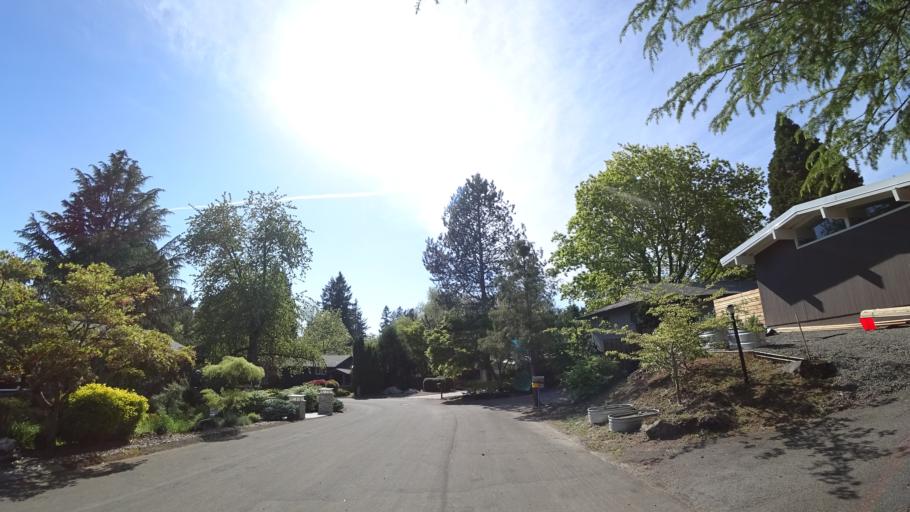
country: US
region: Oregon
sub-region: Washington County
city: West Slope
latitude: 45.4955
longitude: -122.7504
